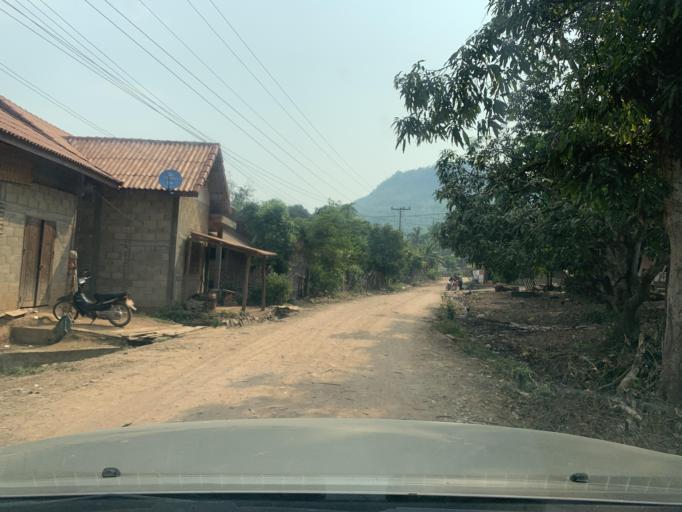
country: LA
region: Louangphabang
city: Louangphabang
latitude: 19.9117
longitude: 102.1360
